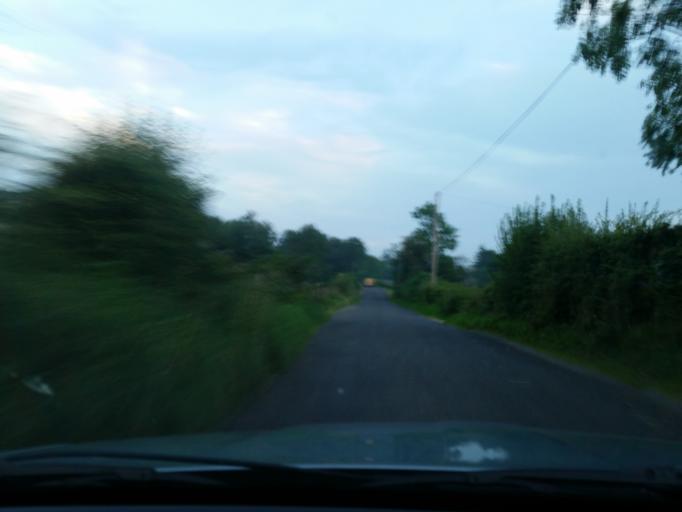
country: GB
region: Northern Ireland
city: Fivemiletown
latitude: 54.3031
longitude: -7.2927
